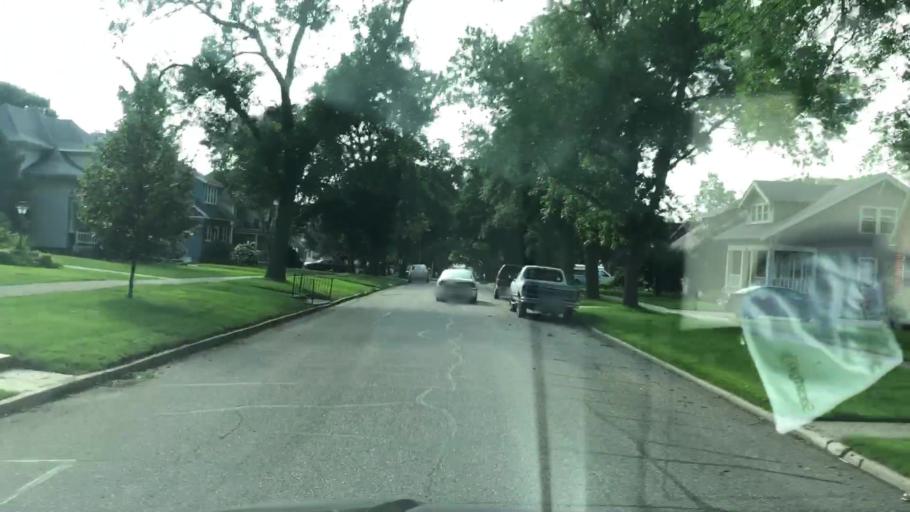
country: US
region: Iowa
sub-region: O'Brien County
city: Sheldon
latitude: 43.1784
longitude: -95.8441
